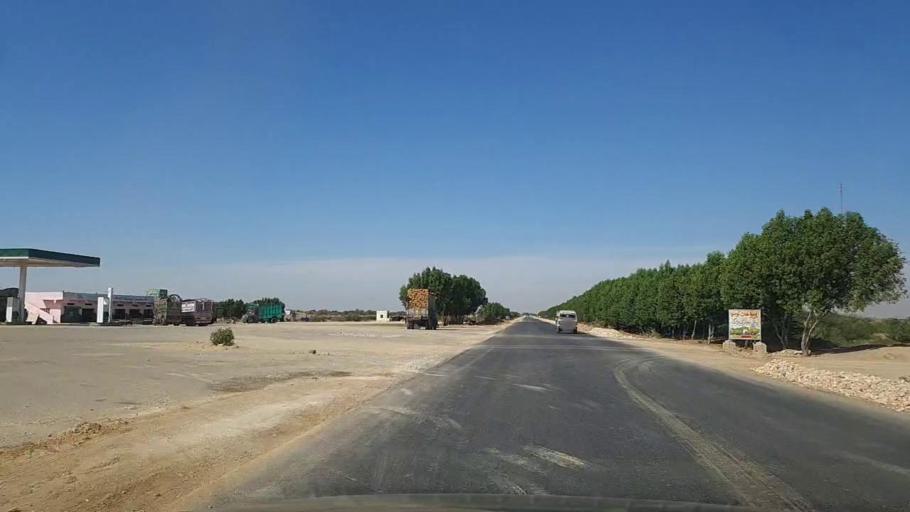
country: PK
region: Sindh
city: Kotri
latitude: 25.2678
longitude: 68.2187
